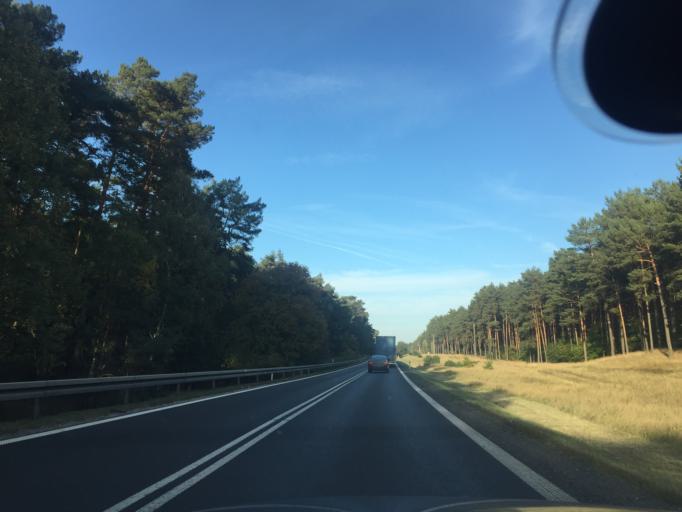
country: PL
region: Kujawsko-Pomorskie
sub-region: Powiat torunski
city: Wielka Nieszawka
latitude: 52.9248
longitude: 18.5005
